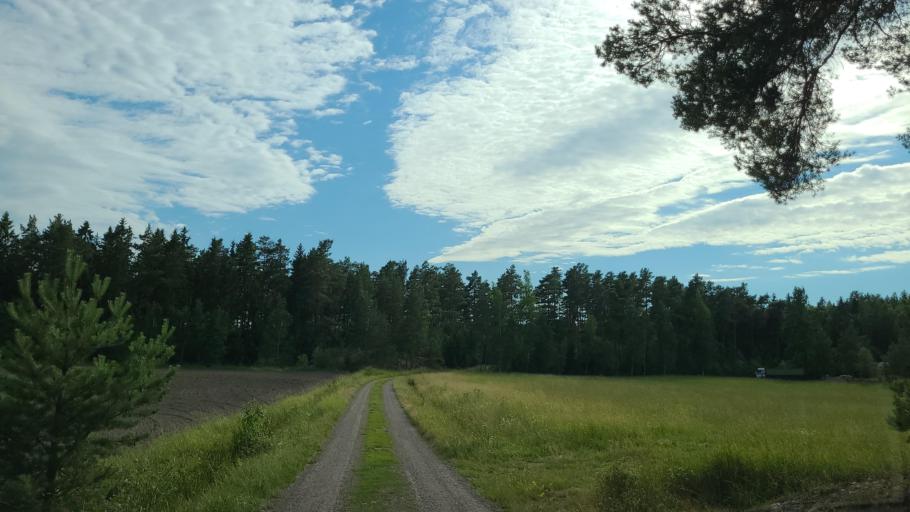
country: FI
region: Varsinais-Suomi
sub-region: Aboland-Turunmaa
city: Nagu
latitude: 60.2865
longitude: 21.9086
